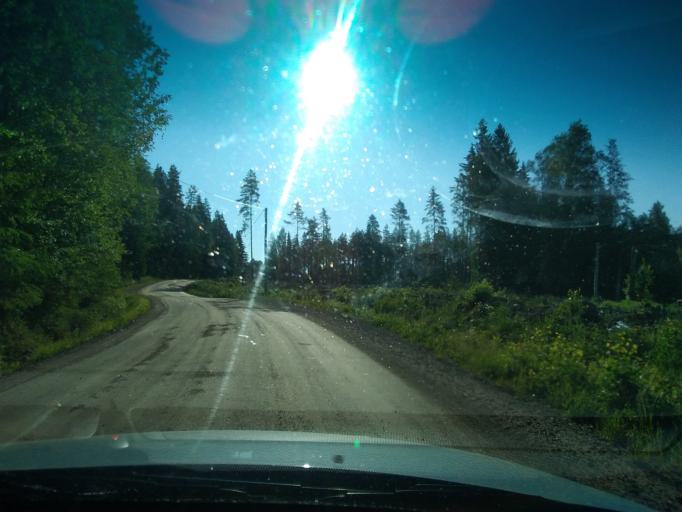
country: FI
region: Haeme
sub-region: Forssa
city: Tammela
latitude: 60.7597
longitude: 23.7703
